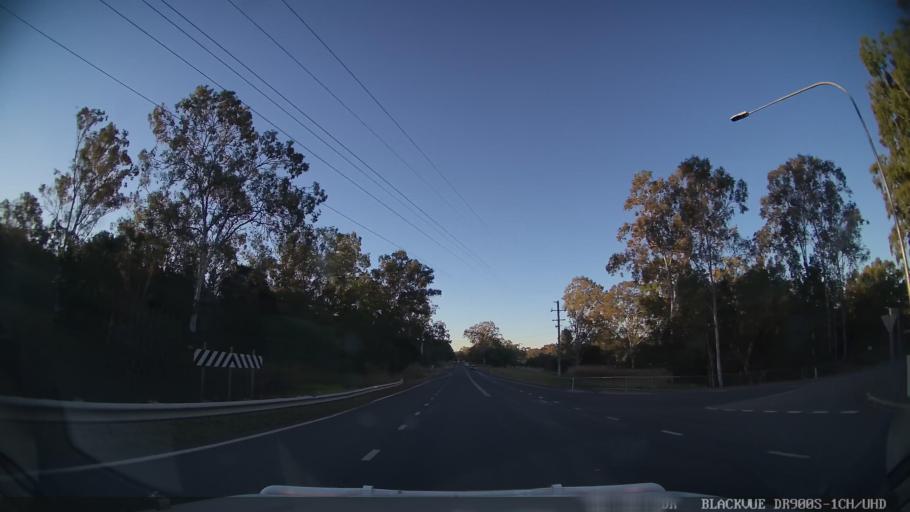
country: AU
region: Queensland
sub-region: Gladstone
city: Toolooa
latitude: -23.9615
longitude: 151.2181
